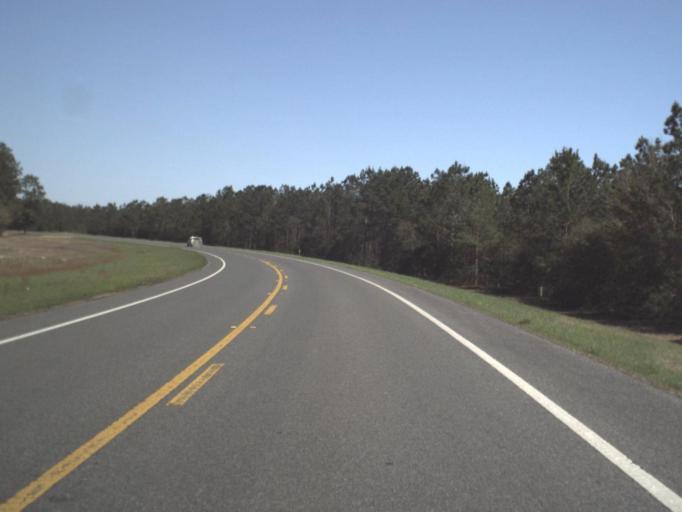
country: US
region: Florida
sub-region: Walton County
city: DeFuniak Springs
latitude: 30.7154
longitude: -86.0156
